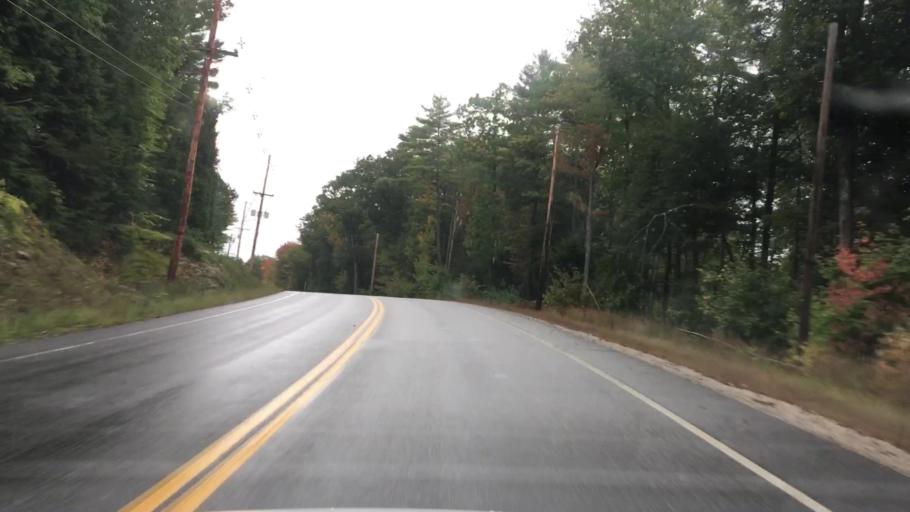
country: US
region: Maine
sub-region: Cumberland County
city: Raymond
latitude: 43.9864
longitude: -70.5506
